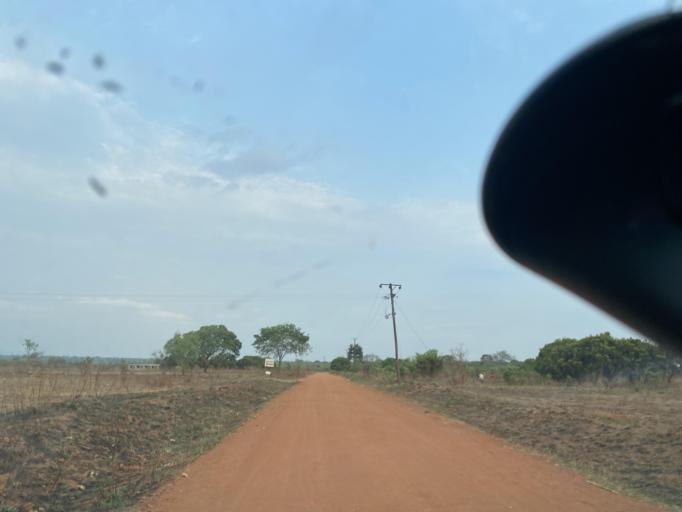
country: ZM
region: Lusaka
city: Chongwe
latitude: -15.2410
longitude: 28.6015
